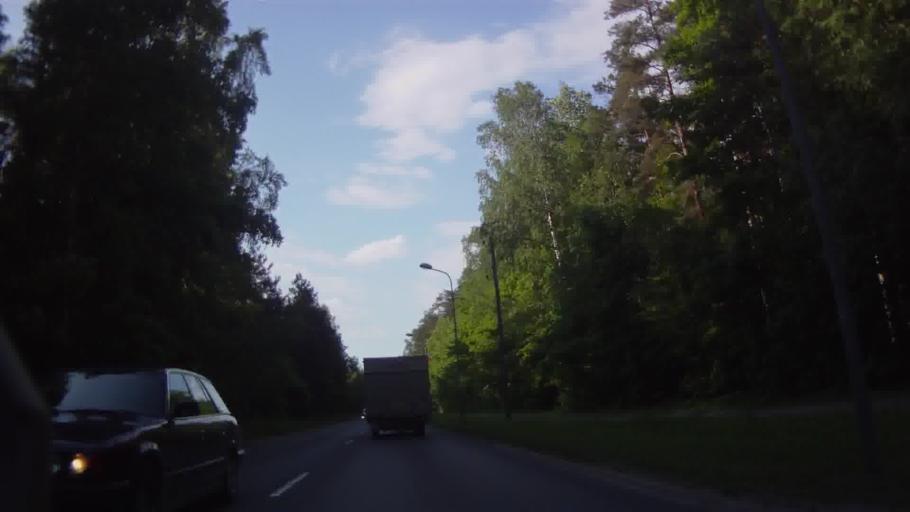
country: LV
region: Stopini
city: Ulbroka
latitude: 56.9638
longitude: 24.2527
